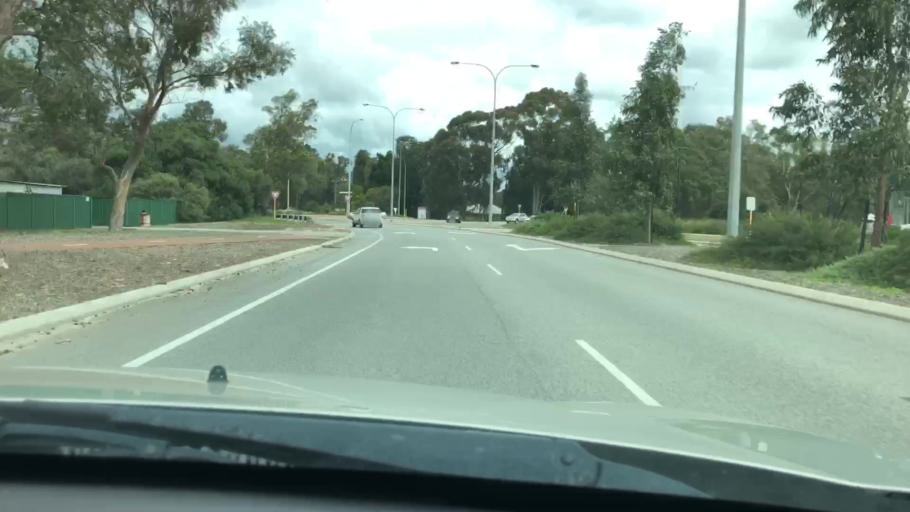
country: AU
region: Western Australia
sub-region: Armadale
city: Seville Grove
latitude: -32.1458
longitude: 115.9737
